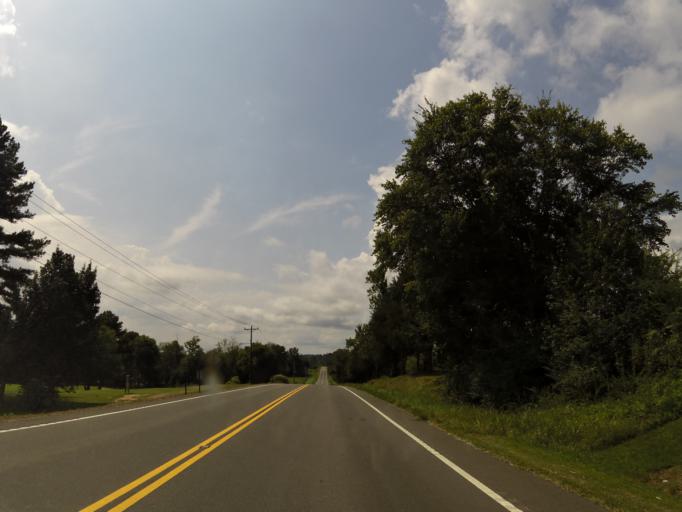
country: US
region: Tennessee
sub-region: Perry County
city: Linden
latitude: 35.7048
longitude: -87.7984
